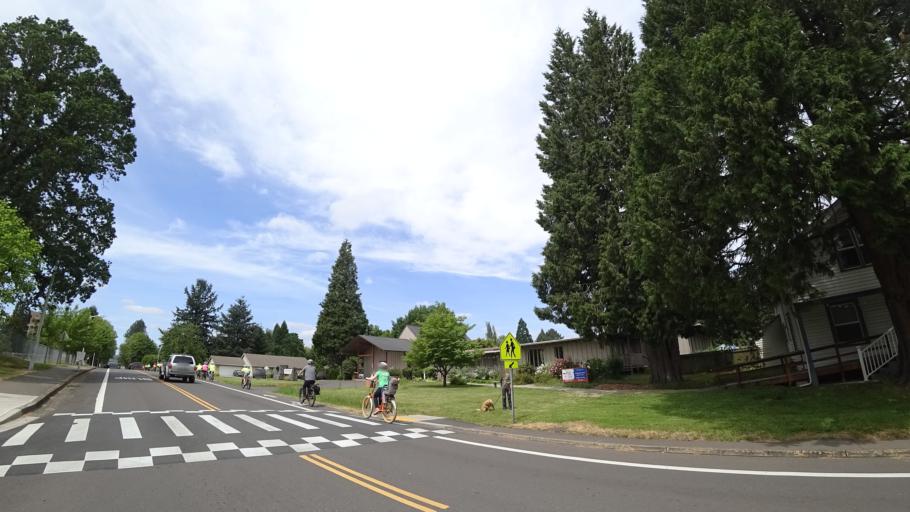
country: US
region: Oregon
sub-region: Washington County
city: Metzger
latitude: 45.4468
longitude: -122.7697
